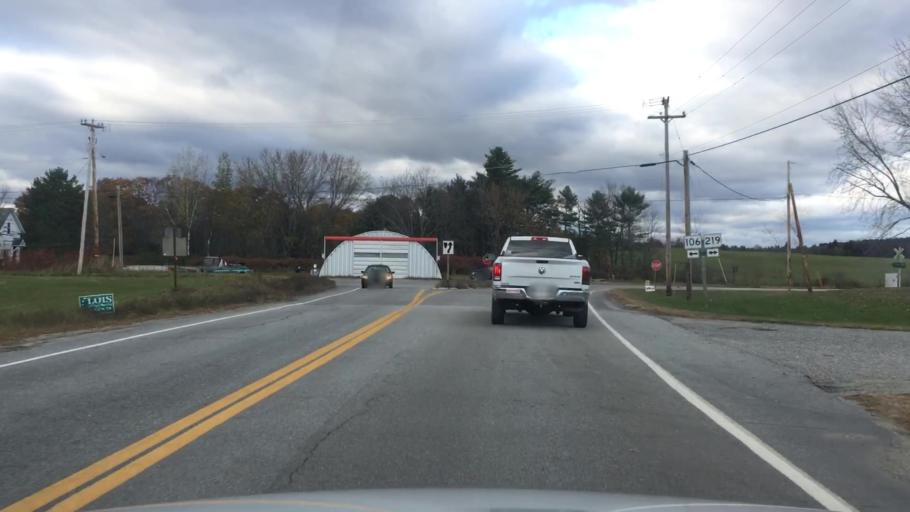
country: US
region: Maine
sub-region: Androscoggin County
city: Leeds
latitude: 44.3427
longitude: -70.1318
